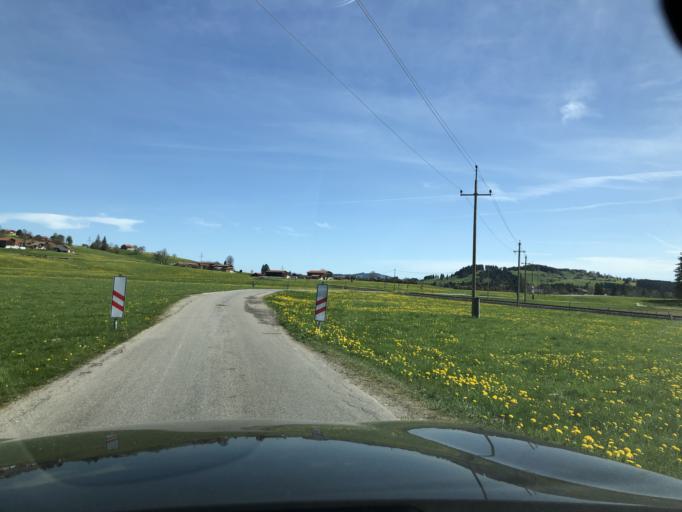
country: DE
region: Bavaria
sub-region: Swabia
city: Seeg
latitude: 47.6390
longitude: 10.6050
